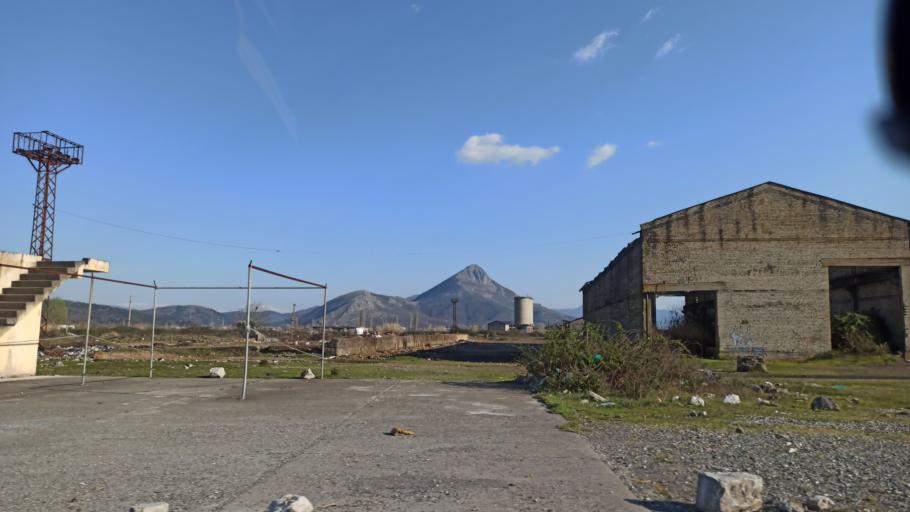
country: AL
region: Shkoder
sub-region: Rrethi i Shkodres
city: Vau i Dejes
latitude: 41.9953
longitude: 19.6114
